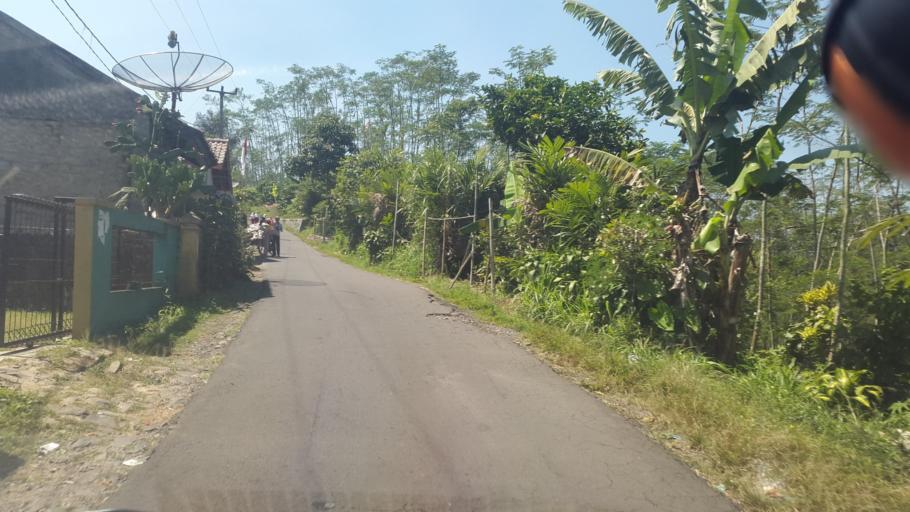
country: ID
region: Banten
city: Kubang
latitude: -6.7709
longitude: 106.6061
